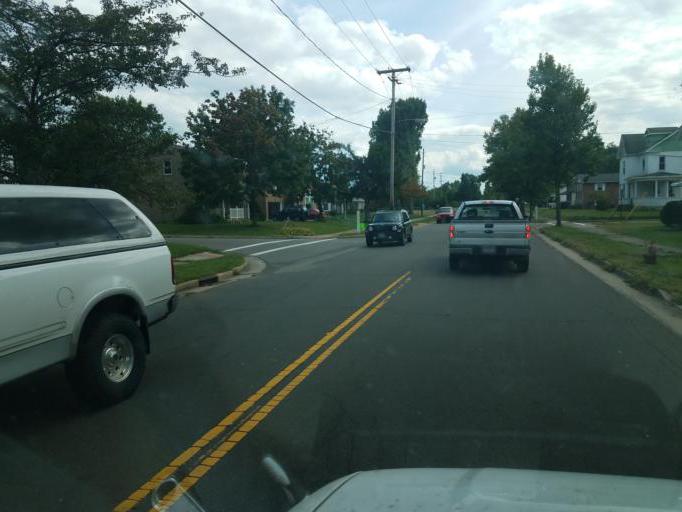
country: US
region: Ohio
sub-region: Stark County
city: Louisville
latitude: 40.8330
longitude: -81.2599
